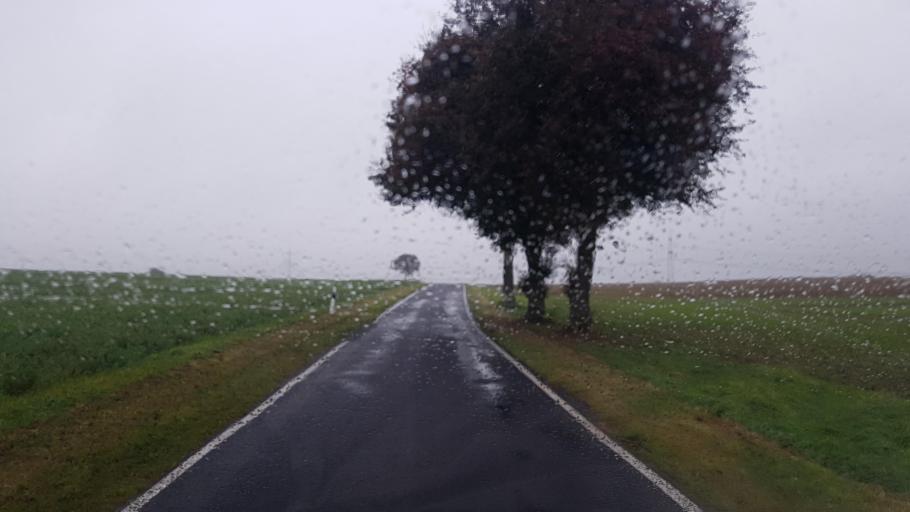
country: DE
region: Brandenburg
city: Furstenwalde
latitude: 52.4144
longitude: 14.0652
